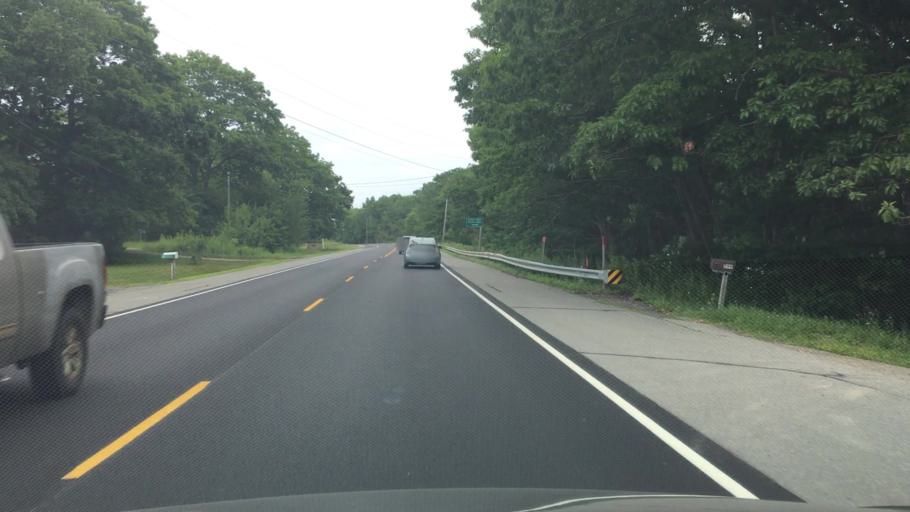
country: US
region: Maine
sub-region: Waldo County
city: Stockton Springs
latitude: 44.5065
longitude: -68.8188
